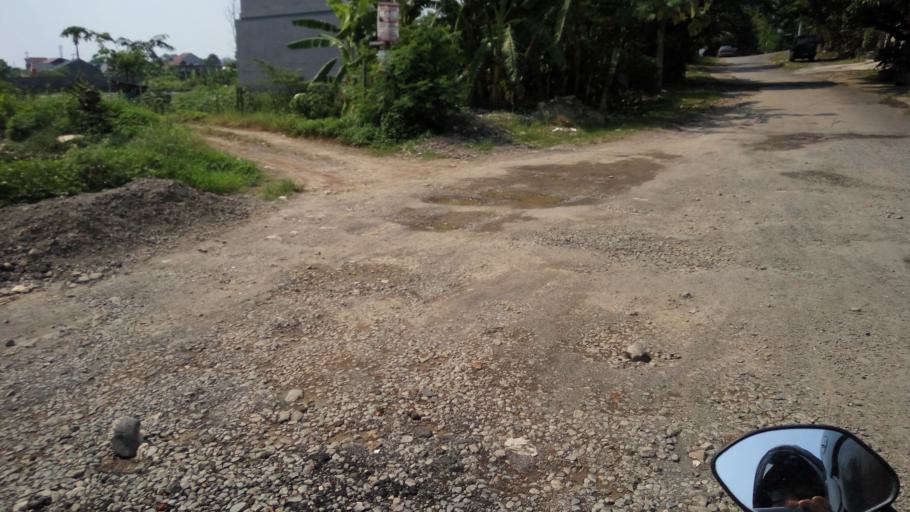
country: ID
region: Central Java
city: Mranggen
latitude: -7.0344
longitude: 110.4719
